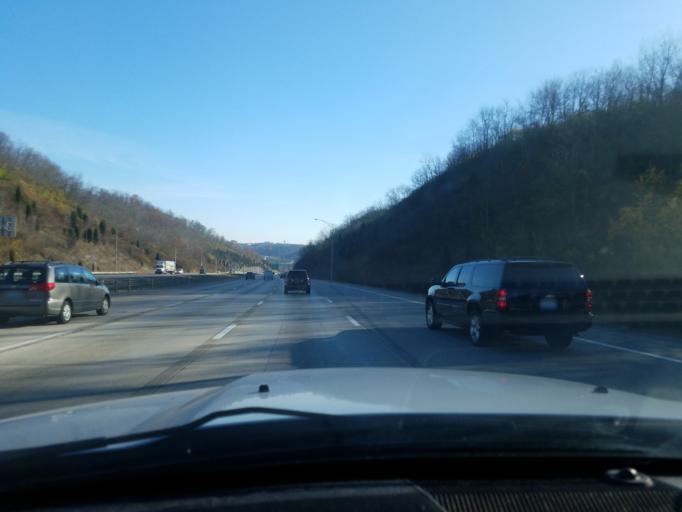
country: US
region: Kentucky
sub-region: Kenton County
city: Taylor Mill
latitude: 39.0216
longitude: -84.5050
